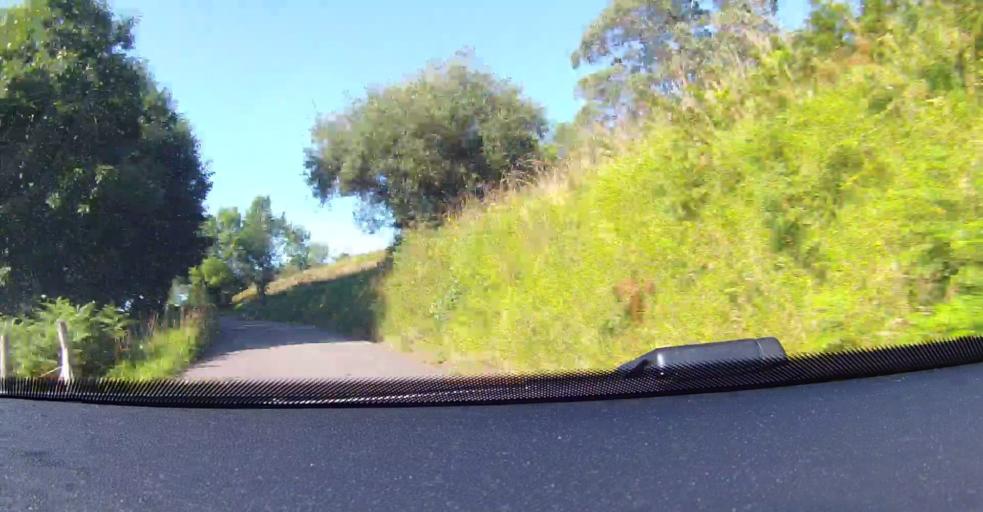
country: ES
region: Asturias
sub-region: Province of Asturias
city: Villaviciosa
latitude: 43.4868
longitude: -5.3921
